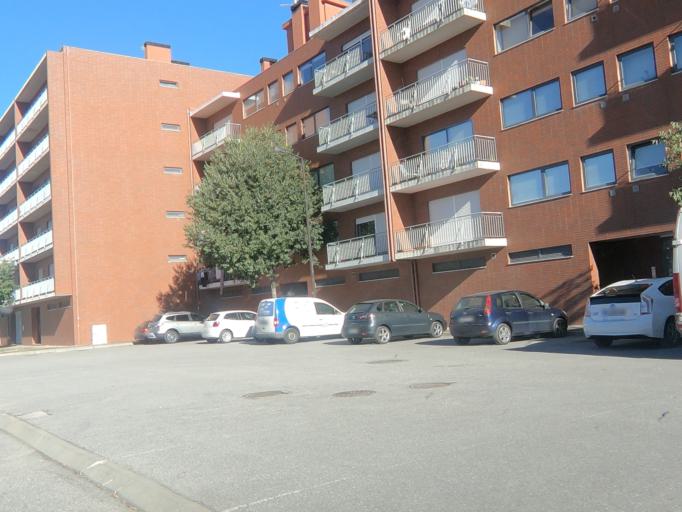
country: PT
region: Vila Real
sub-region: Vila Real
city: Vila Real
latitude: 41.3108
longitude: -7.7432
